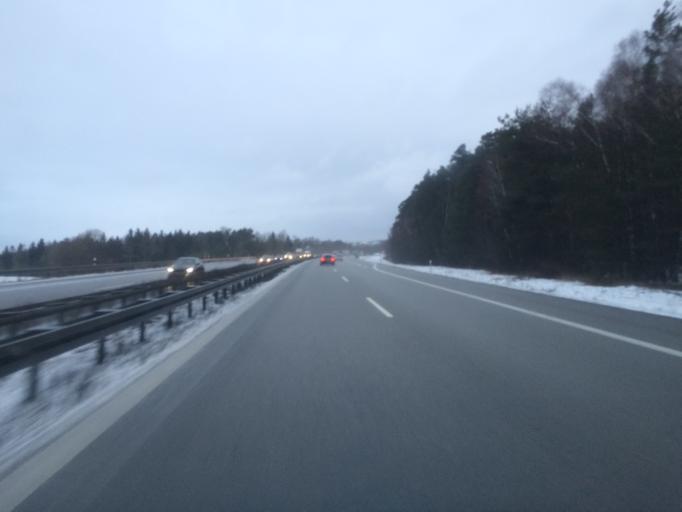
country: DE
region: Bavaria
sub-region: Upper Palatinate
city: Maxhutte-Haidhof
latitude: 49.1674
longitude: 12.1150
